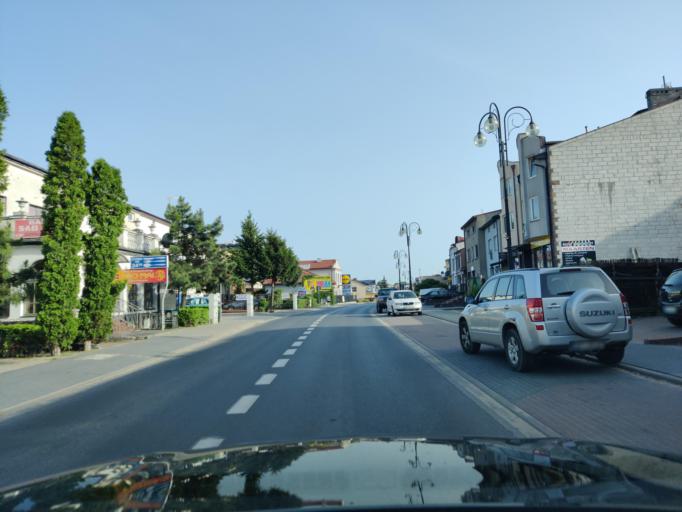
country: PL
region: Masovian Voivodeship
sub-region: Powiat wyszkowski
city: Wyszkow
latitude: 52.5999
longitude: 21.4562
